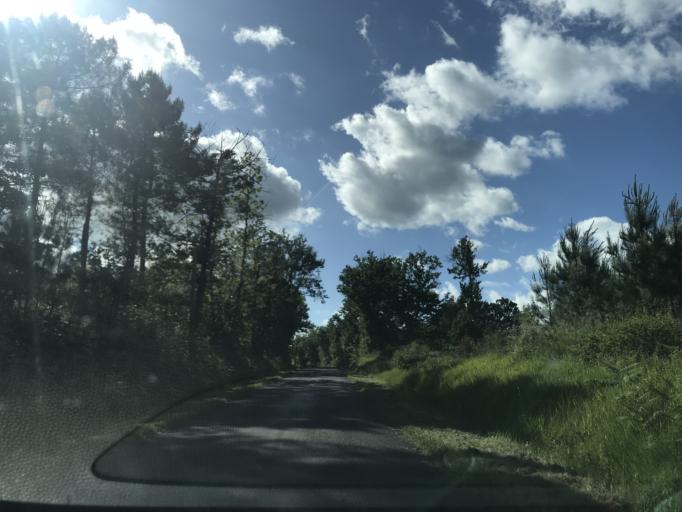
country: FR
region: Poitou-Charentes
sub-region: Departement de la Charente
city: Chalais
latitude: 45.2756
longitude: -0.0344
